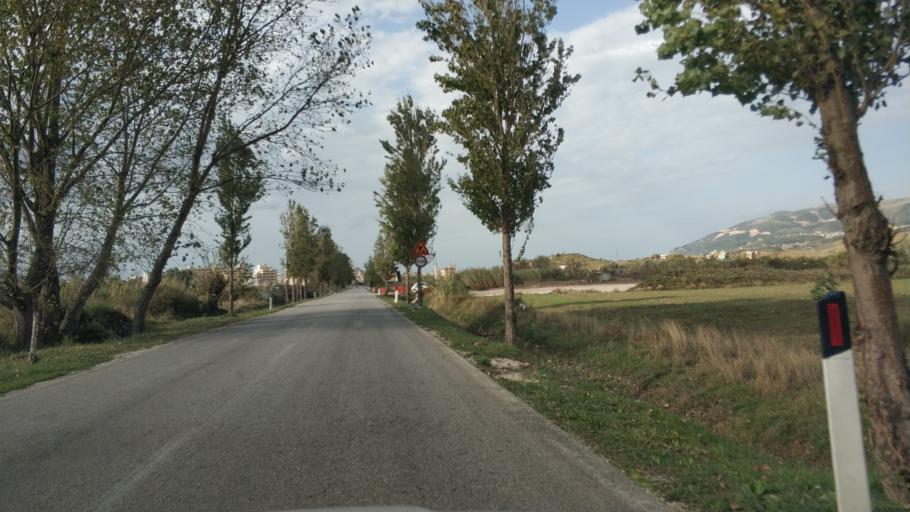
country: AL
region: Vlore
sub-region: Rrethi i Vlores
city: Orikum
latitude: 40.3224
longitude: 19.4811
